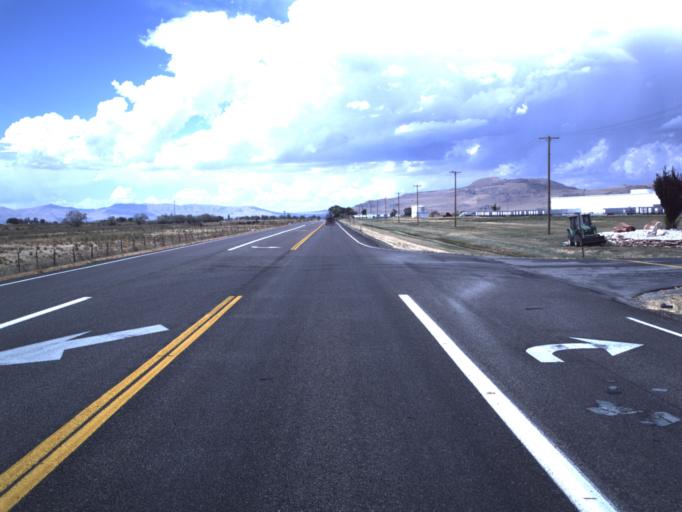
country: US
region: Utah
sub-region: Box Elder County
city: Honeyville
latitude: 41.5573
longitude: -112.1390
